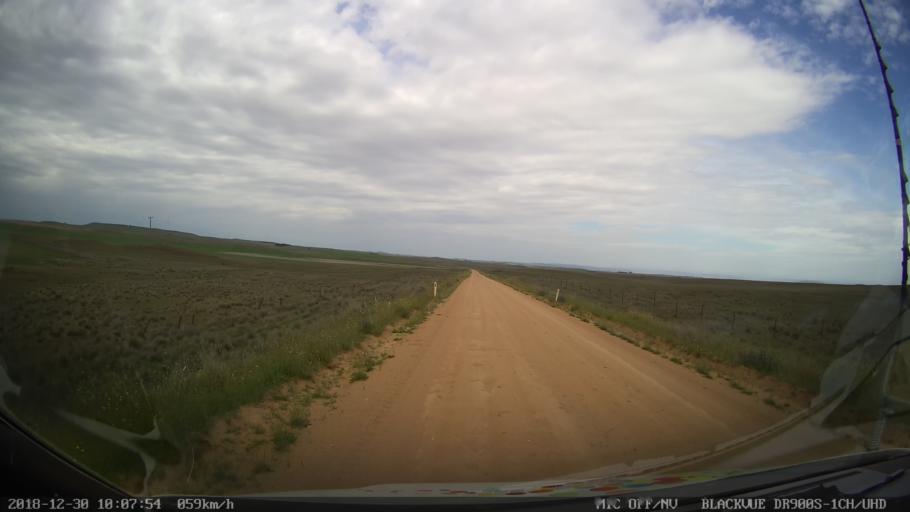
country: AU
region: New South Wales
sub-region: Cooma-Monaro
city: Cooma
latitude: -36.5419
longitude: 149.1186
